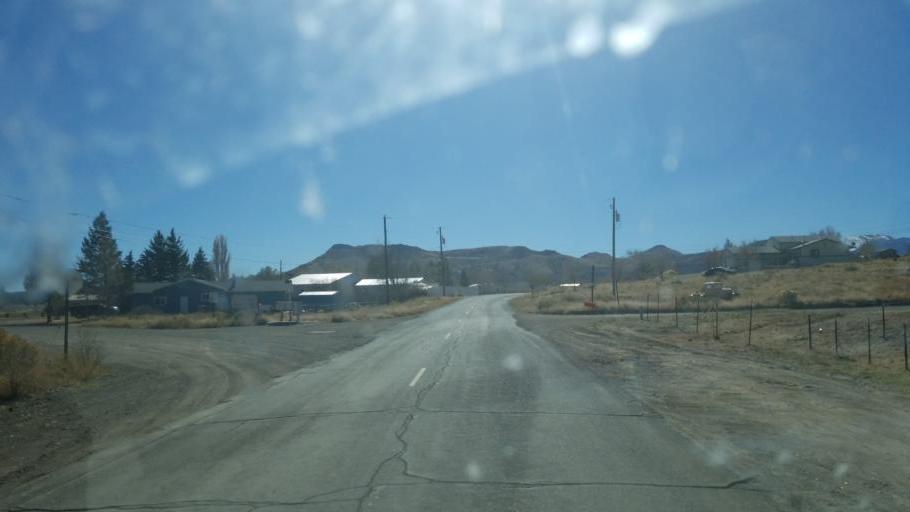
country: US
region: Colorado
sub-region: Rio Grande County
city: Del Norte
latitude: 37.6707
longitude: -106.3464
